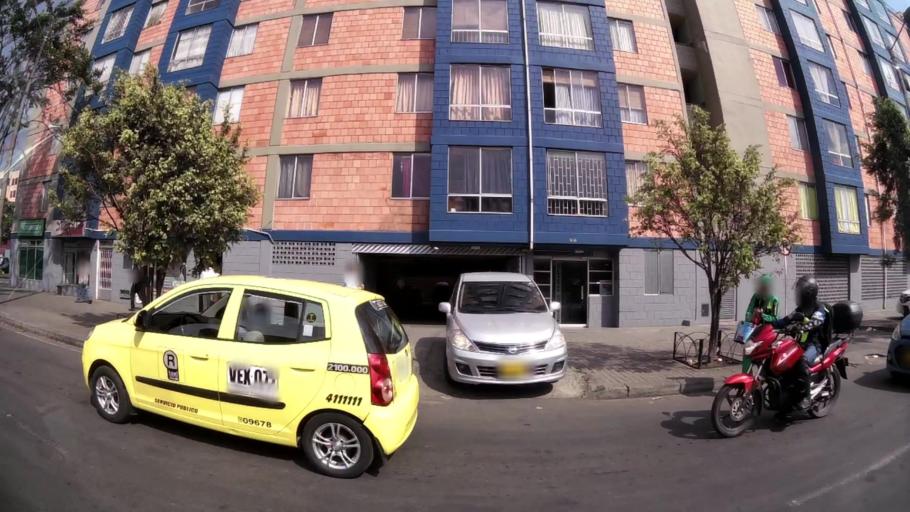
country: CO
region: Bogota D.C.
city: Bogota
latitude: 4.6140
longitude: -74.0838
